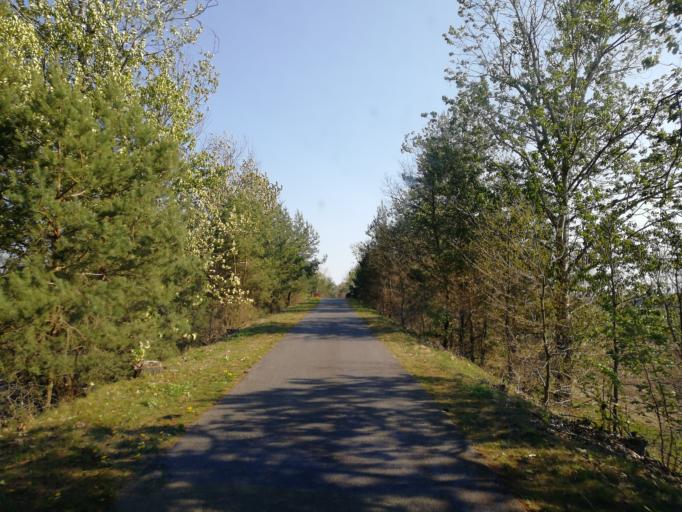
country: DE
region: Brandenburg
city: Bronkow
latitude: 51.6618
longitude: 13.8591
